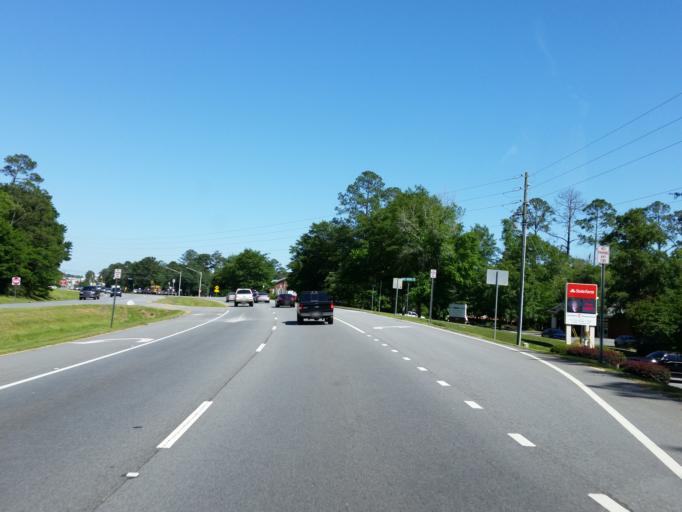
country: US
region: Georgia
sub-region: Lowndes County
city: Remerton
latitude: 30.8808
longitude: -83.3088
